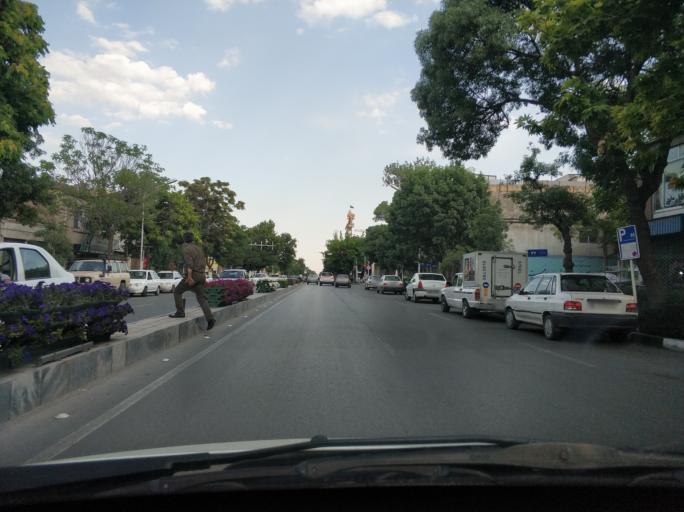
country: IR
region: Razavi Khorasan
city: Mashhad
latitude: 36.2803
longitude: 59.5967
